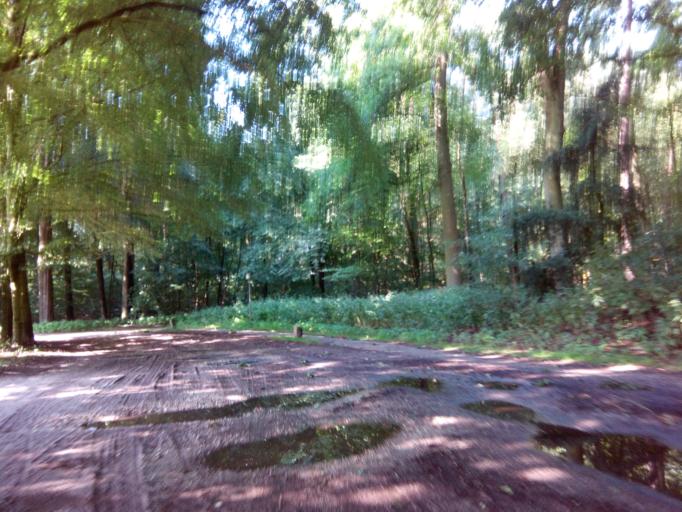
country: NL
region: Utrecht
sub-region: Gemeente Utrechtse Heuvelrug
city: Doorn
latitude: 52.0575
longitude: 5.3272
